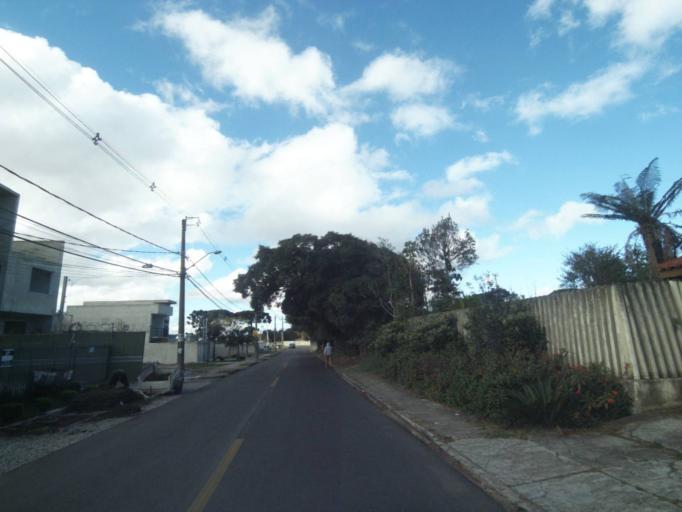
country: BR
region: Parana
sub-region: Sao Jose Dos Pinhais
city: Sao Jose dos Pinhais
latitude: -25.5288
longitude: -49.2852
